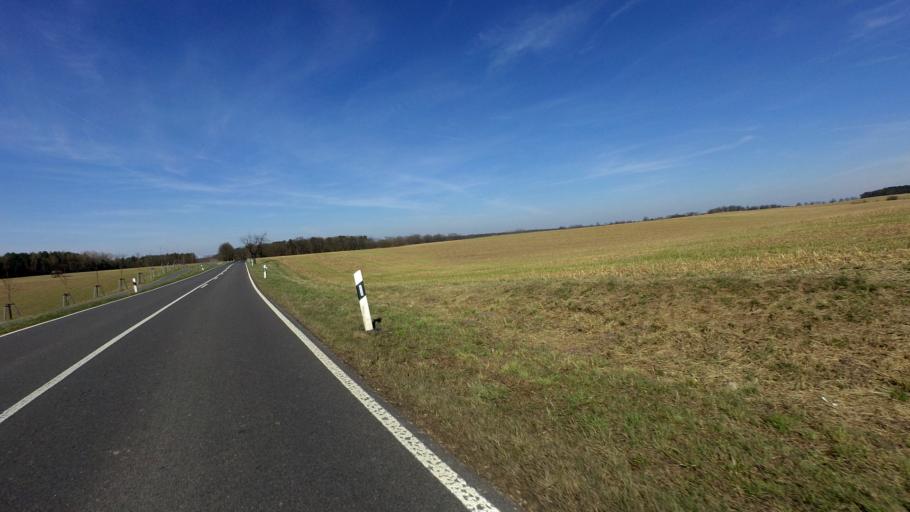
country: DE
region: Brandenburg
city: Furstenwalde
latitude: 52.3943
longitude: 14.0470
